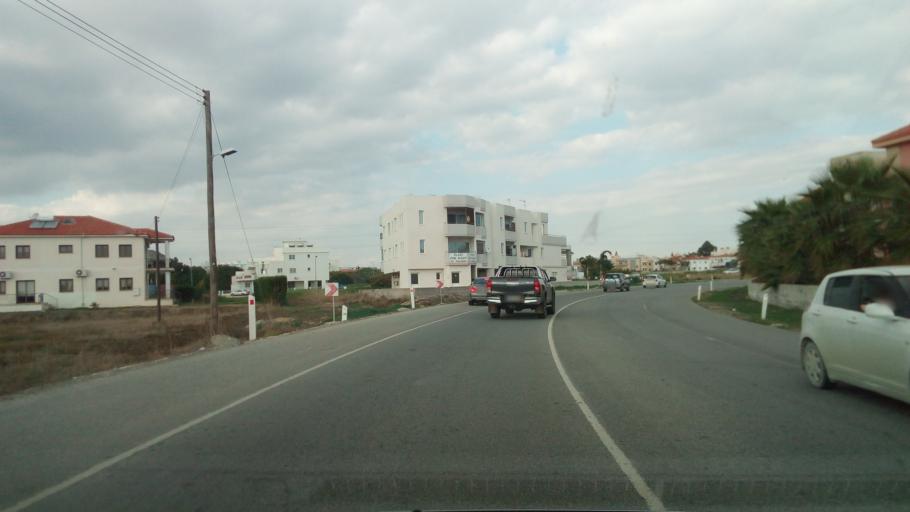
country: CY
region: Larnaka
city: Voroklini
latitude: 34.9740
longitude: 33.6527
